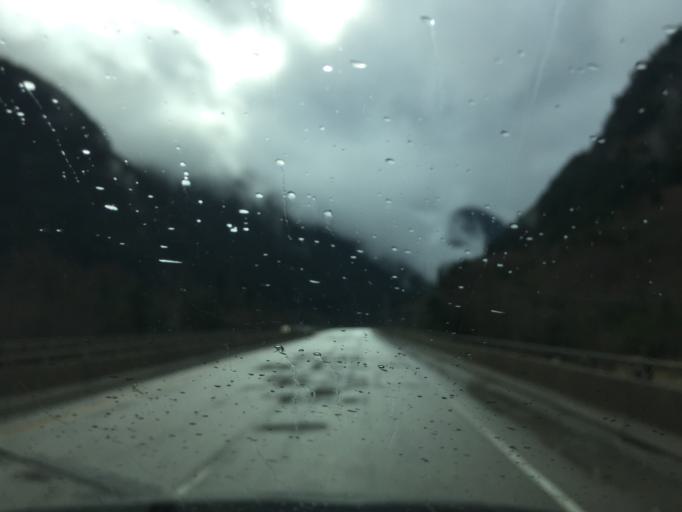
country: CA
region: British Columbia
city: Hope
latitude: 49.4482
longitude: -121.2694
